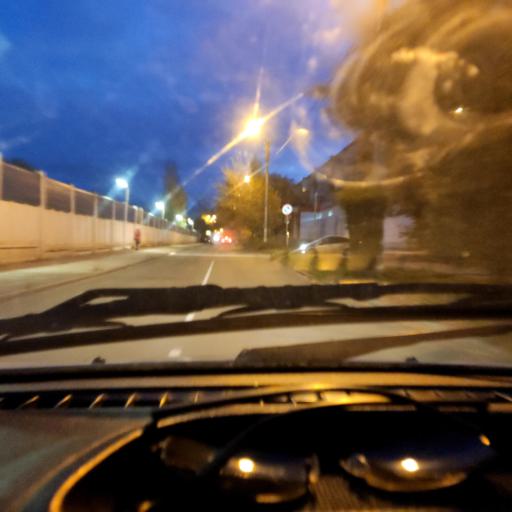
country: RU
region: Samara
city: Zhigulevsk
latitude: 53.4675
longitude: 49.5295
